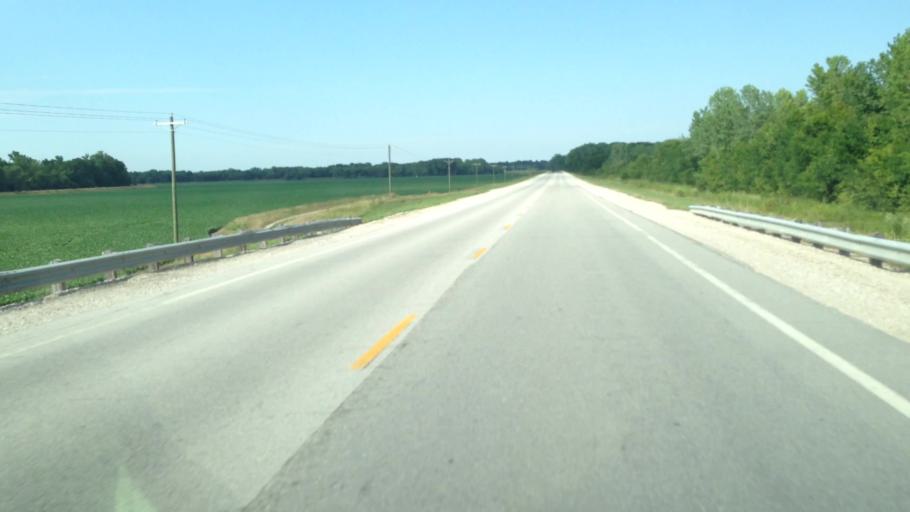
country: US
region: Kansas
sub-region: Neosho County
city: Erie
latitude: 37.5510
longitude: -95.2630
